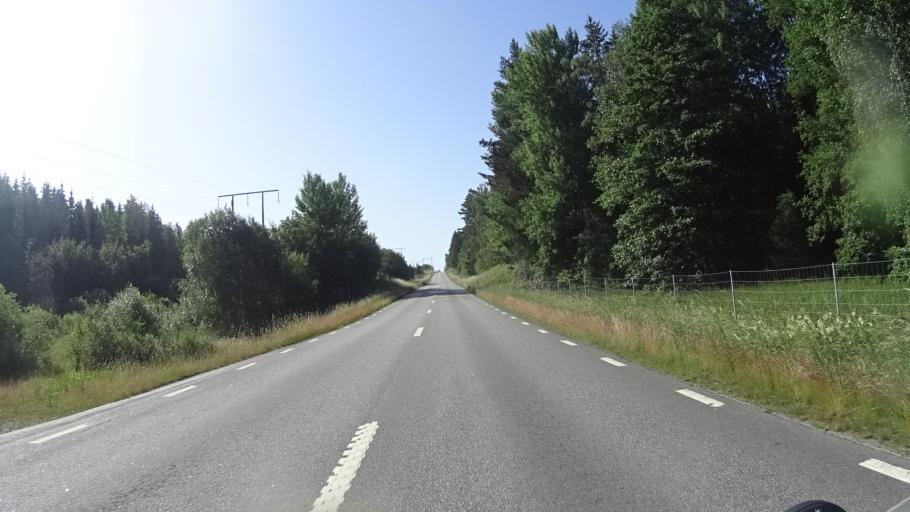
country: SE
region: OEstergoetland
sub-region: Atvidabergs Kommun
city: Atvidaberg
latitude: 58.1589
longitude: 16.0664
